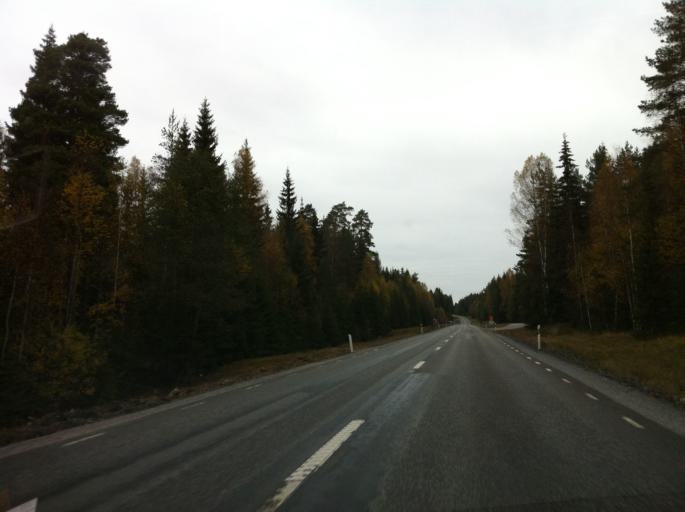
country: SE
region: OErebro
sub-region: Ljusnarsbergs Kommun
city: Kopparberg
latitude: 59.8947
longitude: 15.0174
